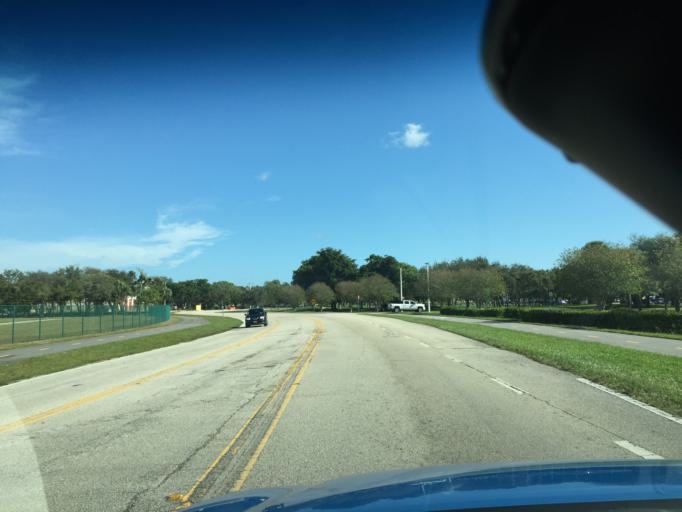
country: US
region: Florida
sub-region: Broward County
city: Pompano Beach
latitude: 26.2421
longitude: -80.1055
